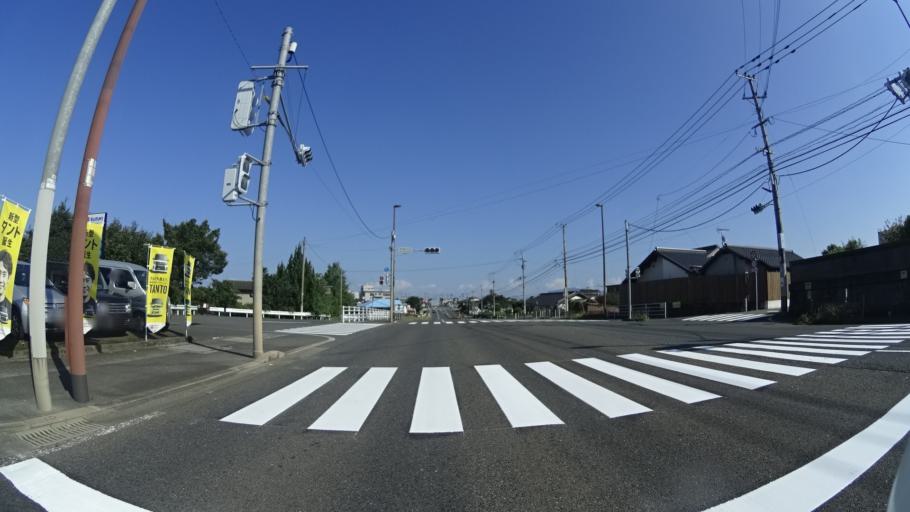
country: JP
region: Fukuoka
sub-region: Buzen-shi
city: Buzen
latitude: 33.6073
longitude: 131.1148
